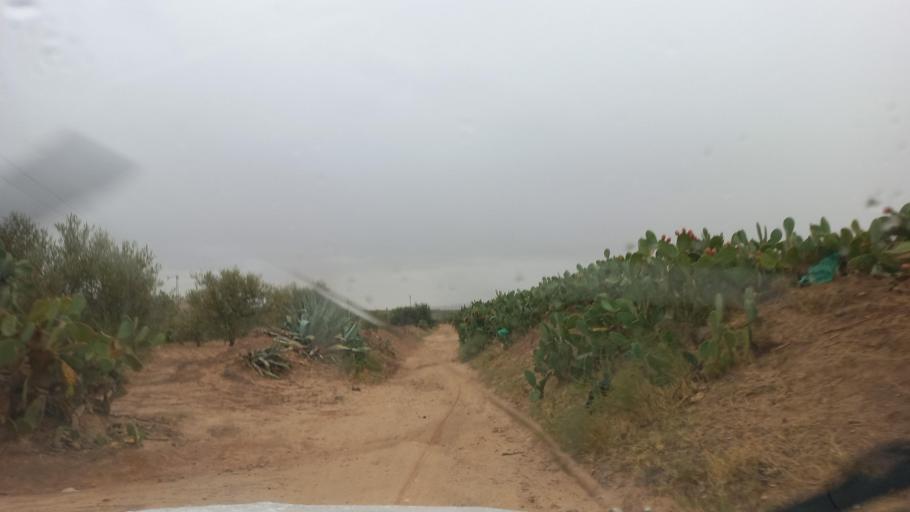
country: TN
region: Al Qasrayn
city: Kasserine
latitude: 35.2735
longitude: 8.9417
